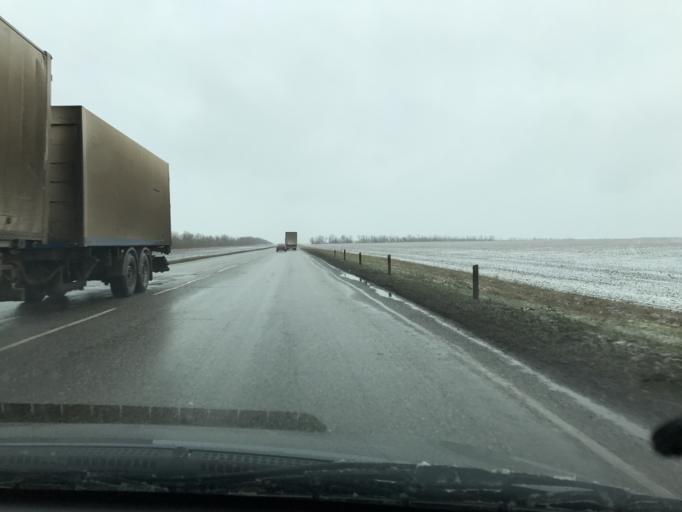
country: RU
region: Rostov
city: Kagal'nitskaya
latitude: 46.8687
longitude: 40.1710
